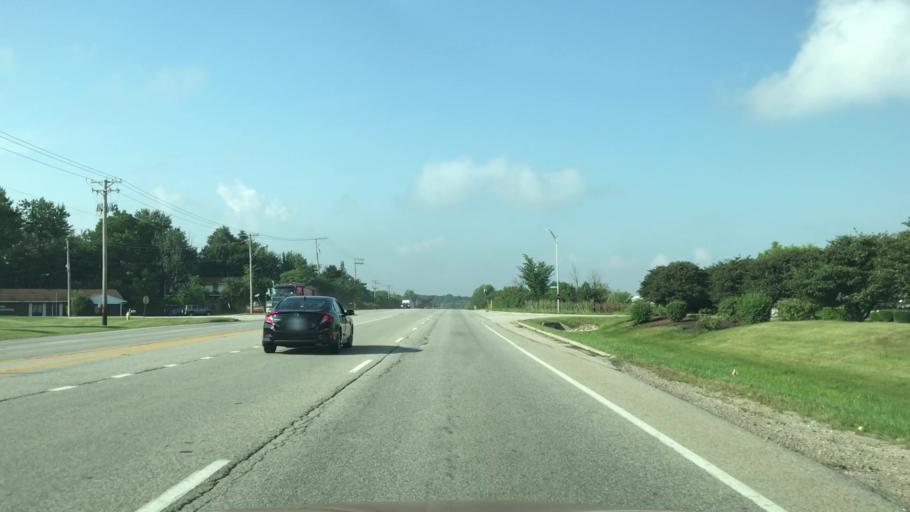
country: US
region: Illinois
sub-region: Will County
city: Bolingbrook
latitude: 41.6853
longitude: -88.0499
